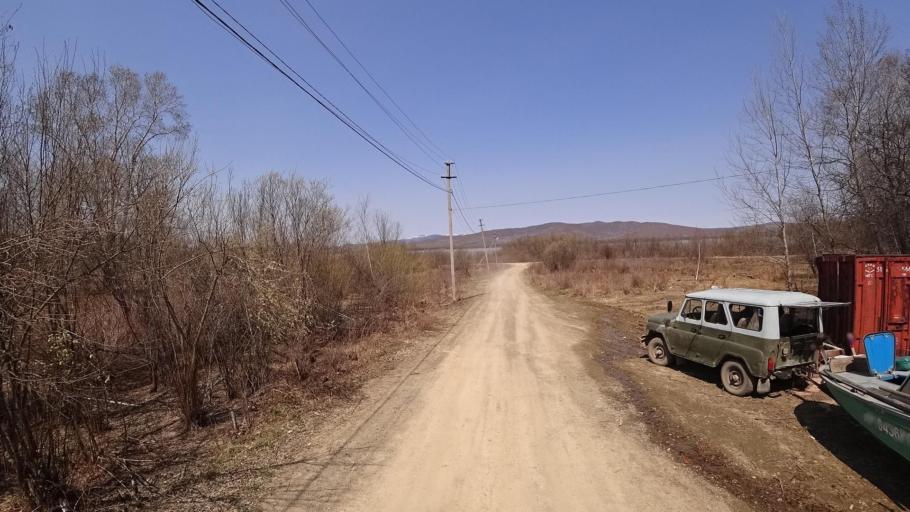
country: RU
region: Khabarovsk Krai
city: Selikhino
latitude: 50.6666
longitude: 137.4046
